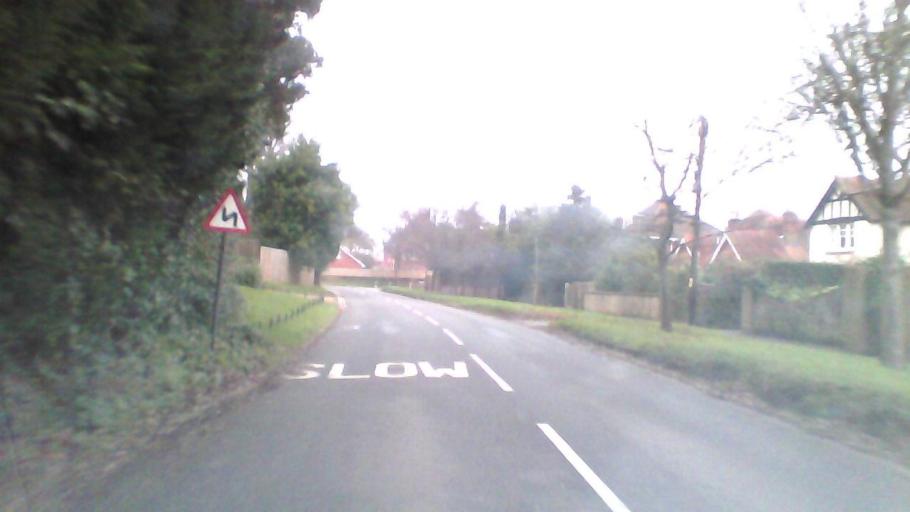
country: GB
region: England
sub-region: Isle of Wight
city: Bembridge
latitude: 50.6872
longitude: -1.0841
